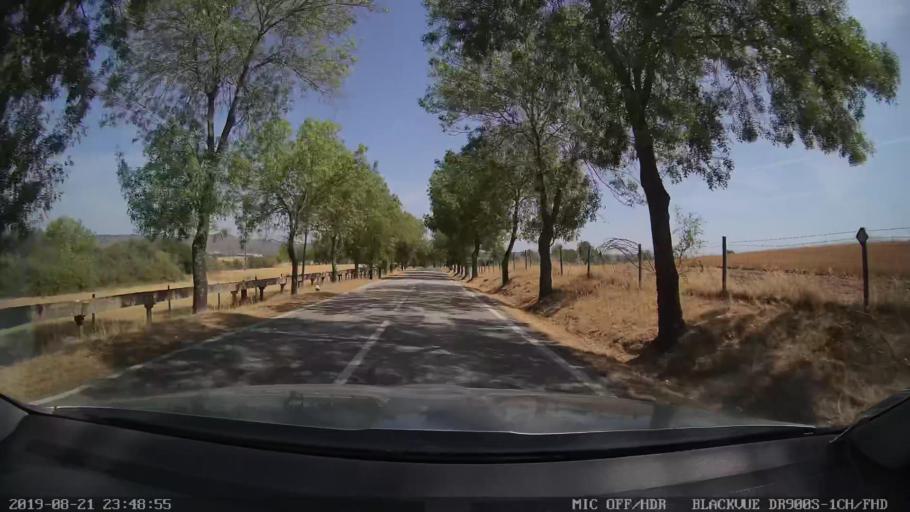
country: PT
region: Castelo Branco
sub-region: Idanha-A-Nova
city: Idanha-a-Nova
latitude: 39.8717
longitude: -7.2524
